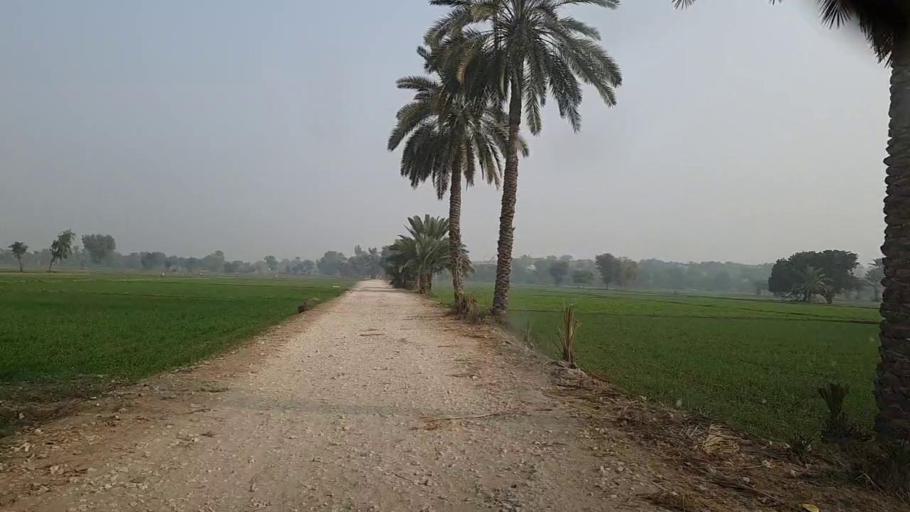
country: PK
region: Sindh
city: Bozdar
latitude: 27.1342
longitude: 68.6545
